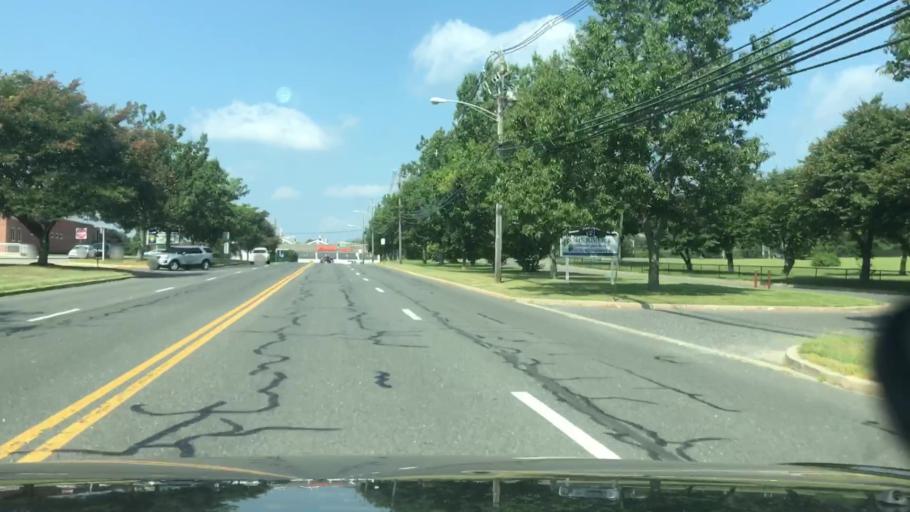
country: US
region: New Jersey
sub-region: Ocean County
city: Toms River
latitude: 39.9875
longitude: -74.1832
